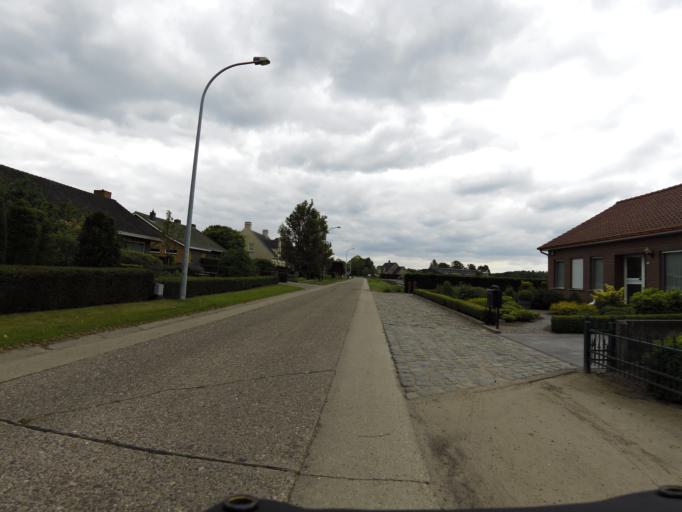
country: BE
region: Flanders
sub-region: Provincie Antwerpen
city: Hoogstraten
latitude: 51.4781
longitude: 4.8124
